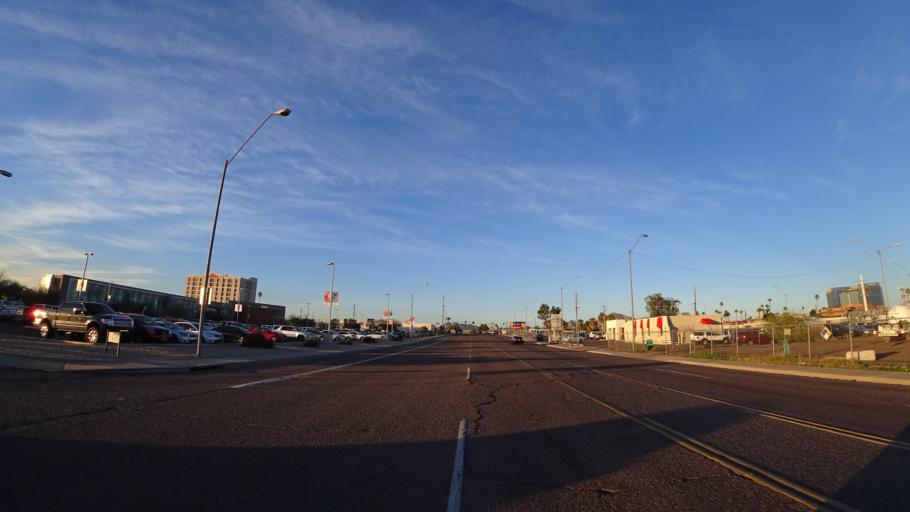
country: US
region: Arizona
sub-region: Maricopa County
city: Tempe Junction
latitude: 33.4493
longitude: -111.9954
